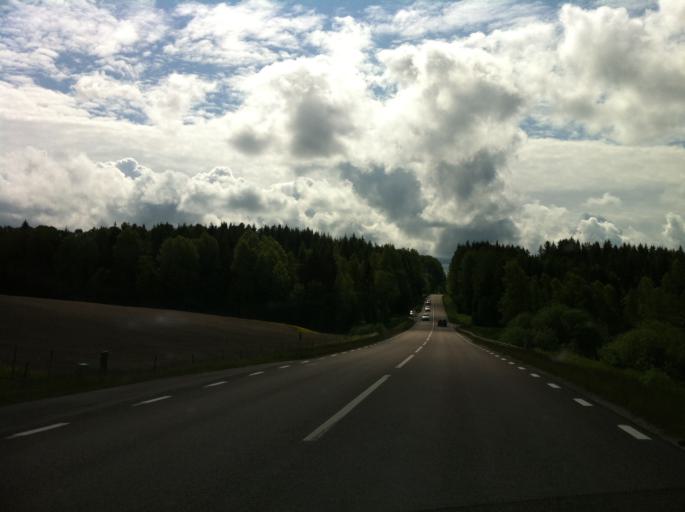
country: SE
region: Vaermland
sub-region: Karlstads Kommun
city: Edsvalla
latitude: 59.5537
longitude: 13.1907
